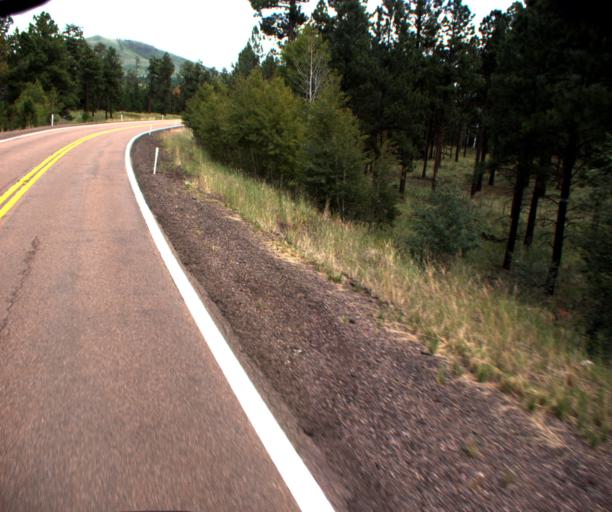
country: US
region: Arizona
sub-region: Apache County
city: Eagar
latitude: 34.0685
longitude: -109.4863
